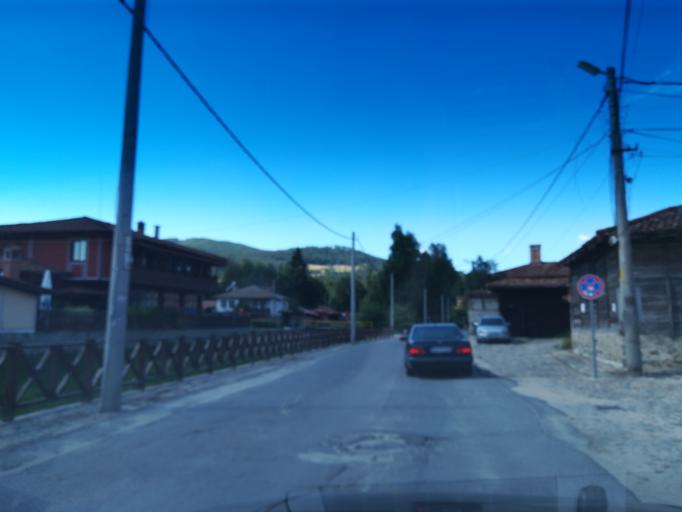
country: BG
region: Sofiya
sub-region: Obshtina Koprivshtitsa
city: Koprivshtitsa
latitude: 42.6355
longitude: 24.3614
